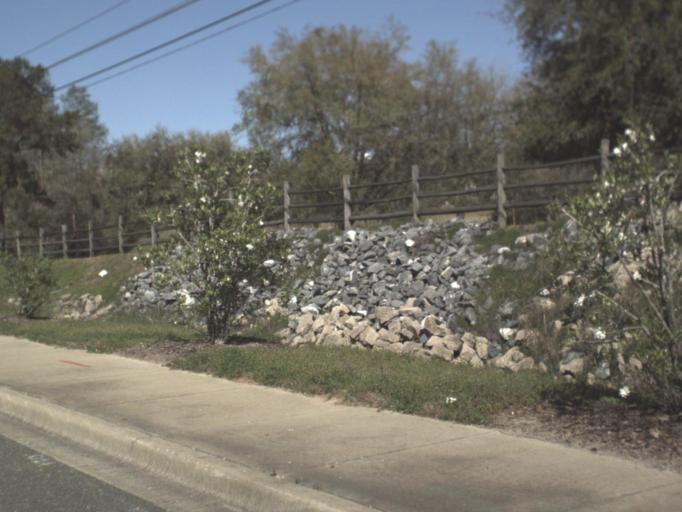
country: US
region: Florida
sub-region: Leon County
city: Tallahassee
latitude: 30.4364
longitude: -84.2265
